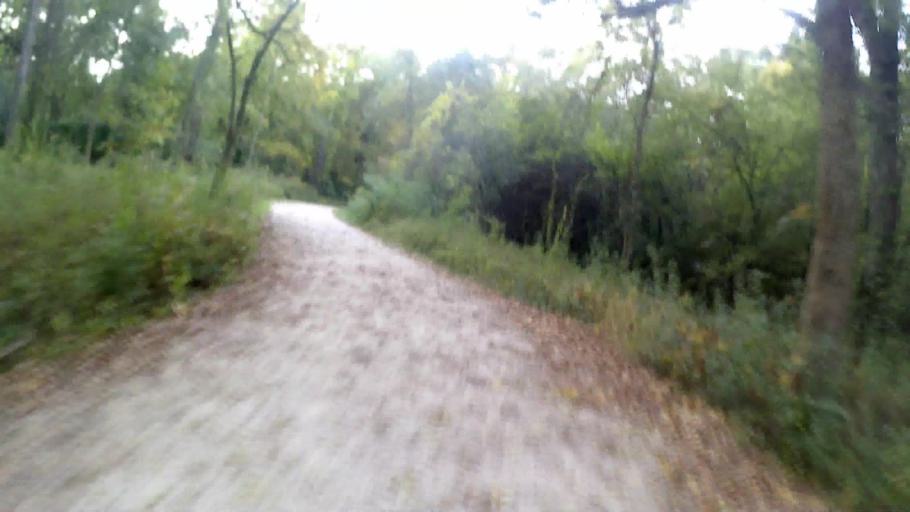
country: US
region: Illinois
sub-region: DuPage County
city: Naperville
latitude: 41.8176
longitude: -88.1256
